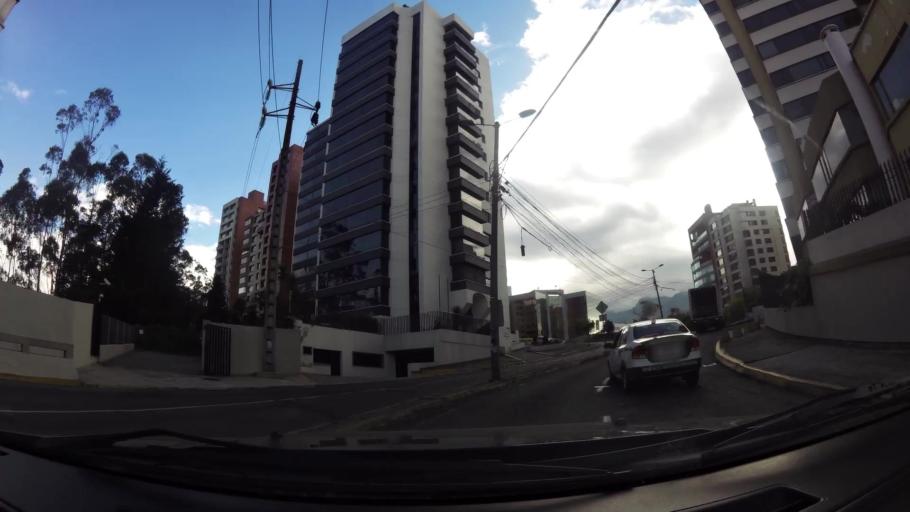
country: EC
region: Pichincha
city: Quito
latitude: -0.1935
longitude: -78.4754
